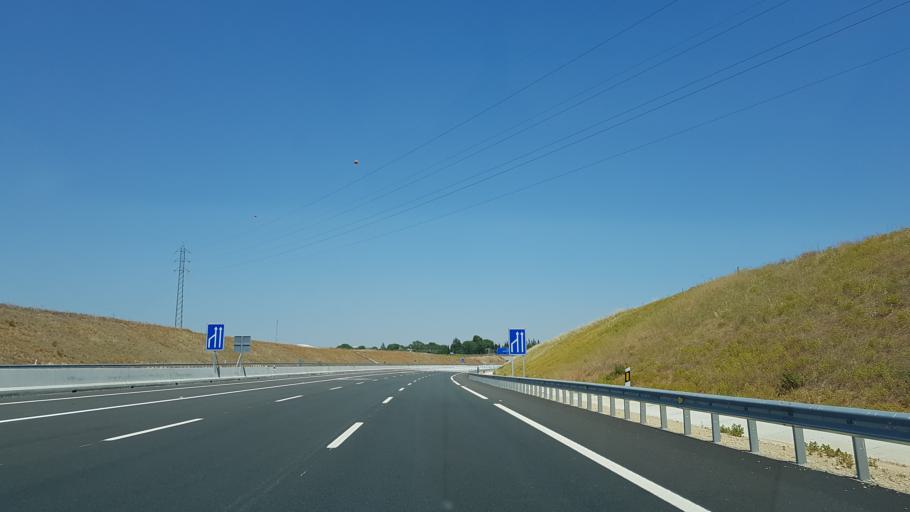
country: ES
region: Andalusia
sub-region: Provincia de Sevilla
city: Coria del Rio
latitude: 37.3006
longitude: -6.0633
